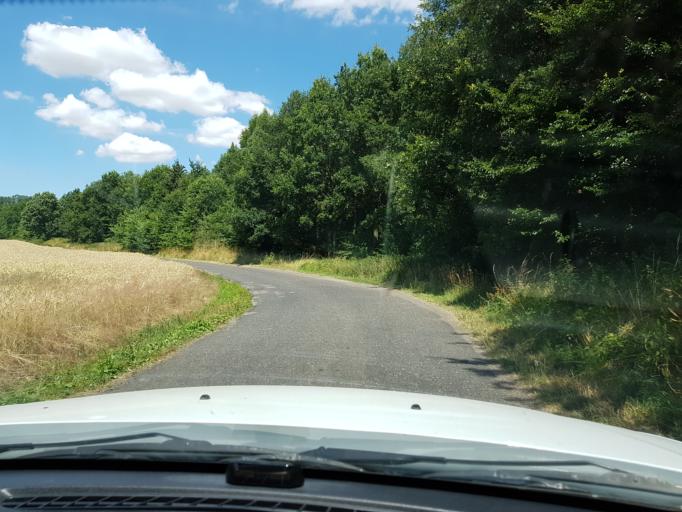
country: PL
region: West Pomeranian Voivodeship
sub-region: Powiat mysliborski
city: Barlinek
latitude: 52.9817
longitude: 15.1284
